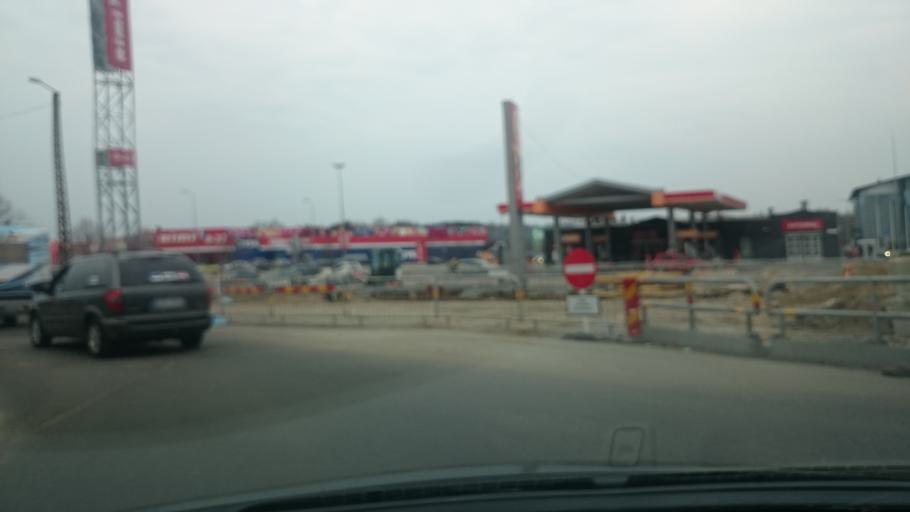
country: EE
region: Harju
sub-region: Saue vald
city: Laagri
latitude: 59.4236
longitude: 24.6471
